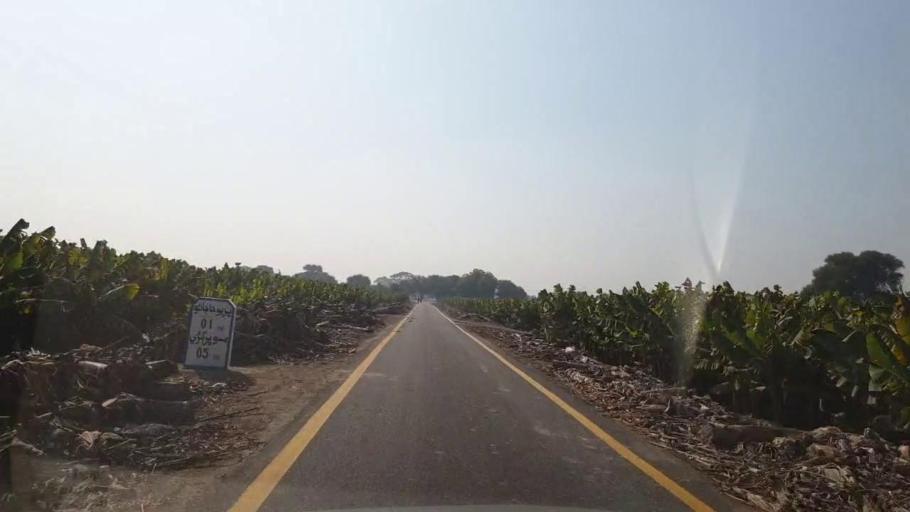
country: PK
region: Sindh
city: Matiari
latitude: 25.5328
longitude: 68.4922
